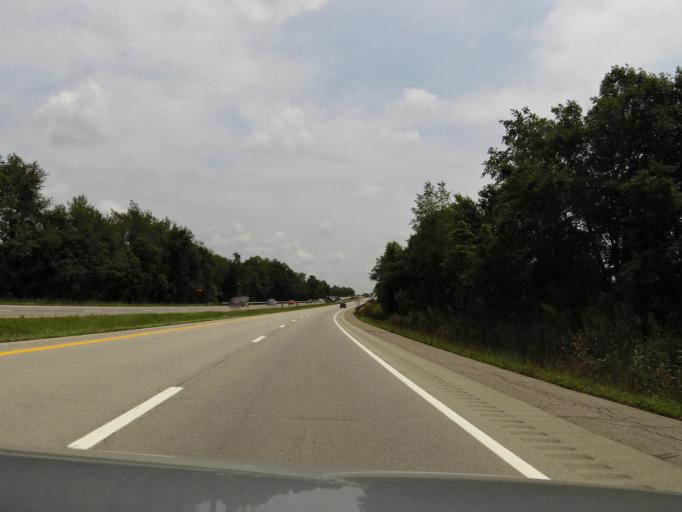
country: US
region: Kentucky
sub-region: Hardin County
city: Elizabethtown
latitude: 37.6480
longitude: -85.9093
